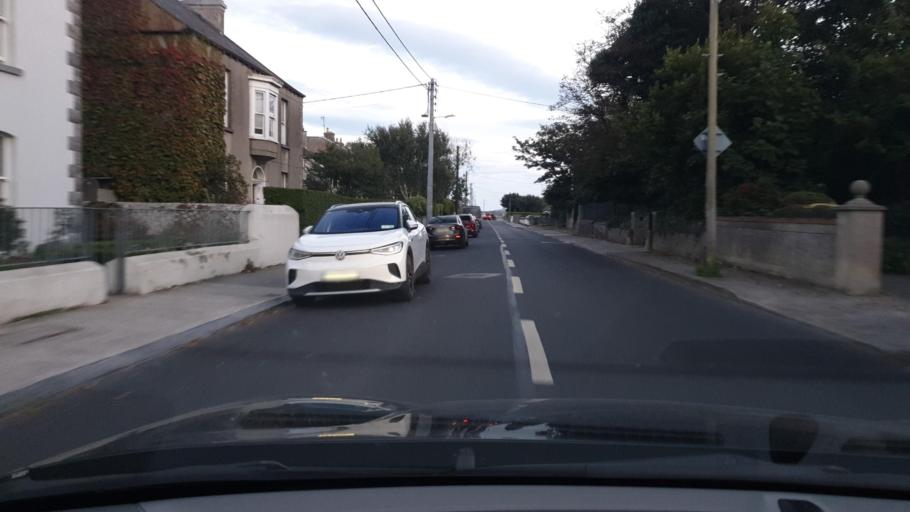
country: IE
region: Leinster
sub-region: Fingal County
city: Skerries
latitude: 53.5743
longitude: -6.1036
